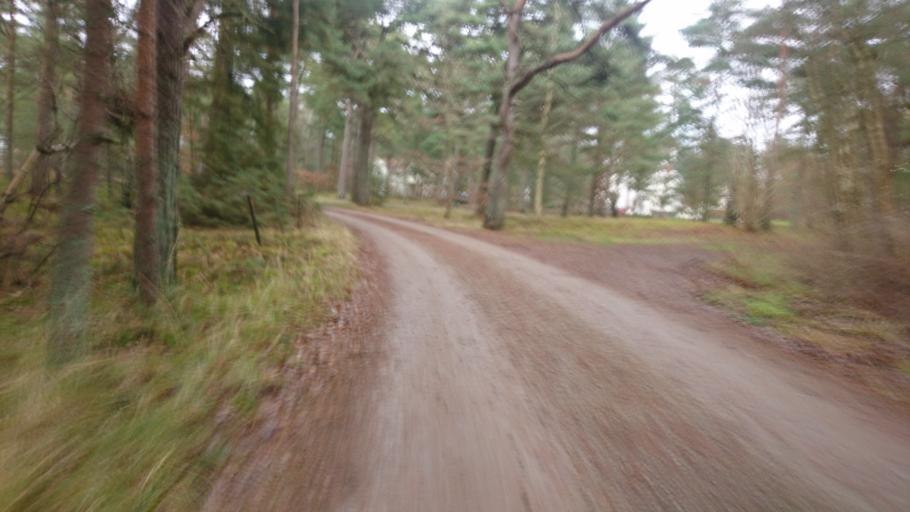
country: SE
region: Skane
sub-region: Vellinge Kommun
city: Ljunghusen
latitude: 55.3883
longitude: 12.9215
